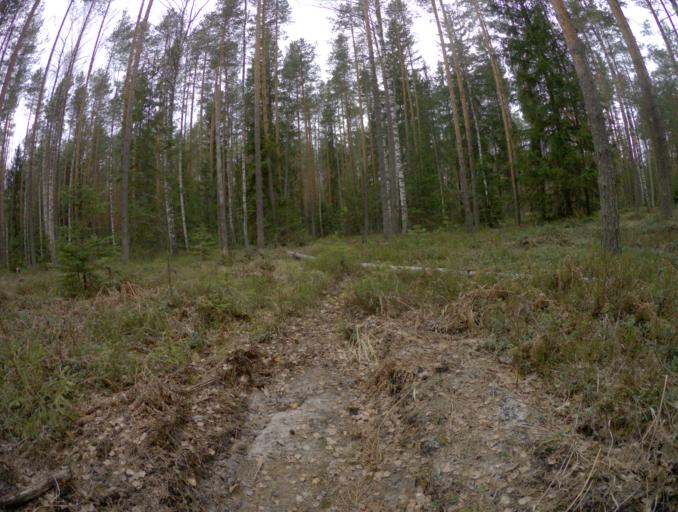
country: RU
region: Vladimir
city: Raduzhnyy
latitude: 55.9315
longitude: 40.2862
